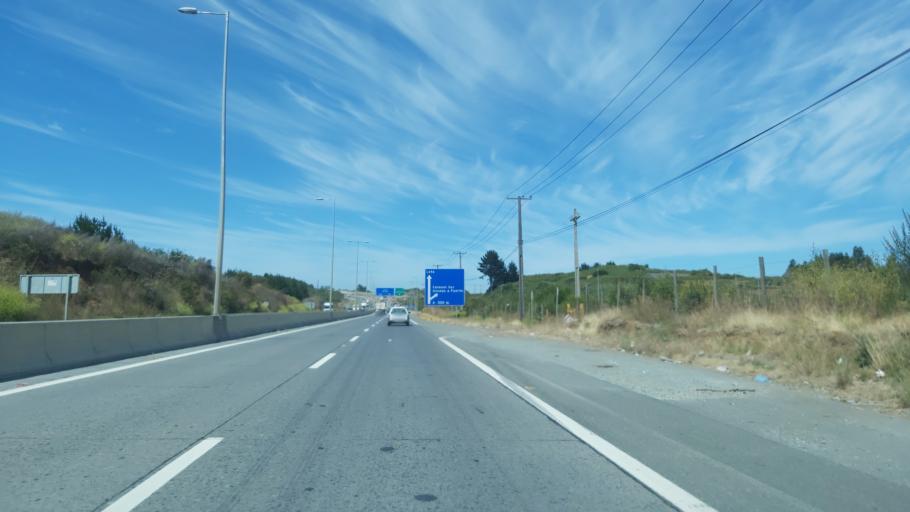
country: CL
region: Biobio
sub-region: Provincia de Concepcion
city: Coronel
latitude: -37.0415
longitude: -73.1371
